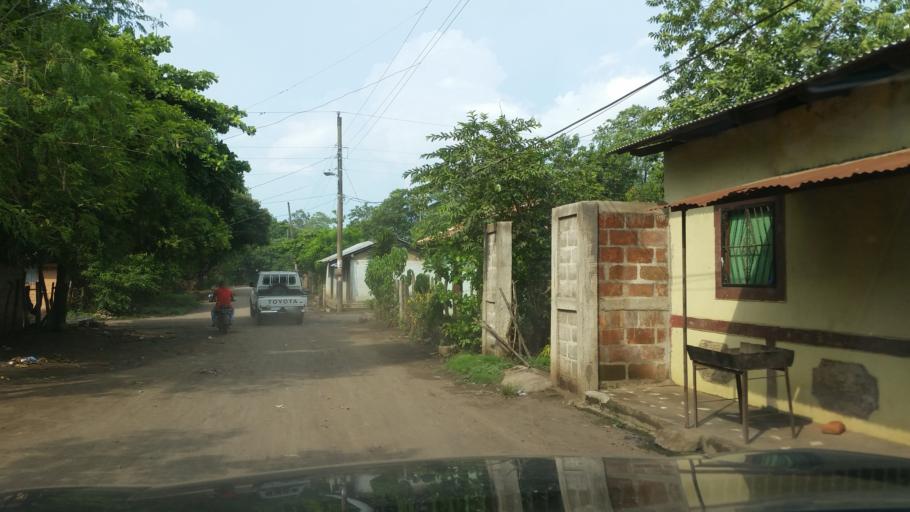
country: NI
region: Chinandega
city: Puerto Morazan
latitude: 12.7650
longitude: -87.1310
